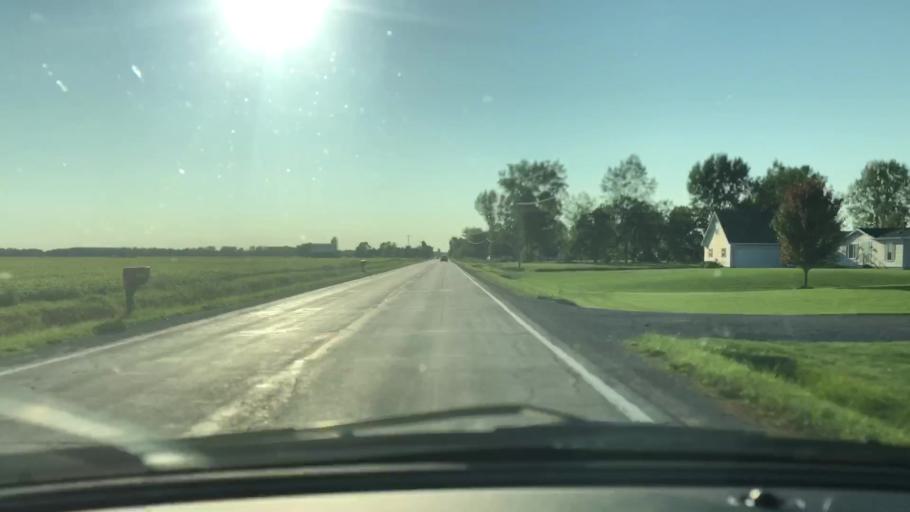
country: US
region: Michigan
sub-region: Bay County
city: Auburn
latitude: 43.6400
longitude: -84.1112
